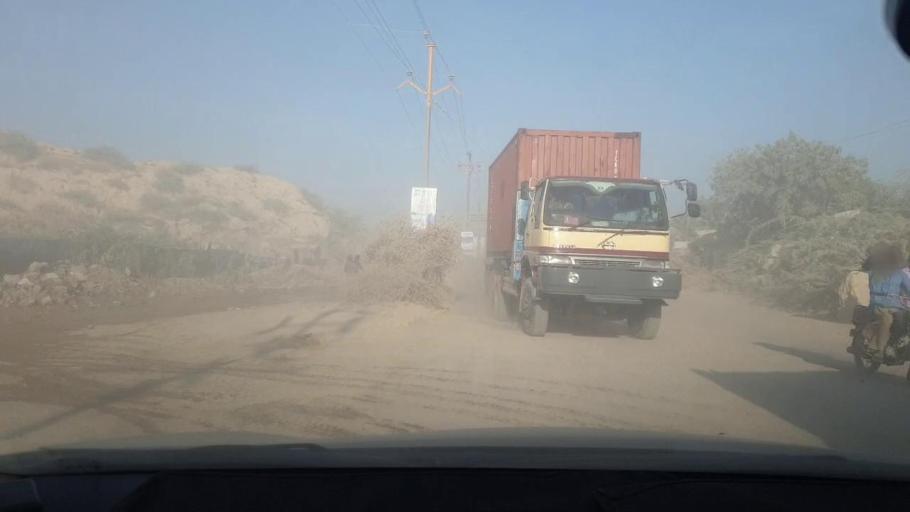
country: PK
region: Sindh
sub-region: Karachi District
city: Karachi
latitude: 24.9762
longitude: 67.0389
